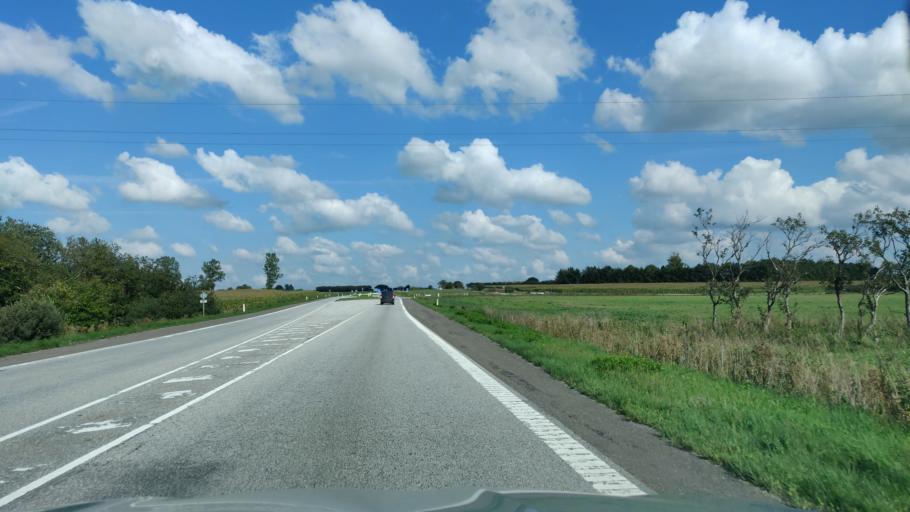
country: DK
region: North Denmark
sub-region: Vesthimmerland Kommune
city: Aars
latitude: 56.8070
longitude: 9.6496
